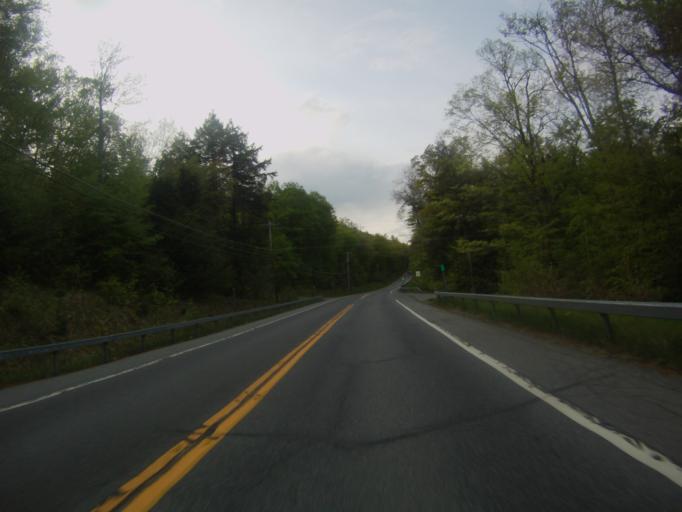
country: US
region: New York
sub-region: Essex County
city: Ticonderoga
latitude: 43.7646
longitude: -73.4900
